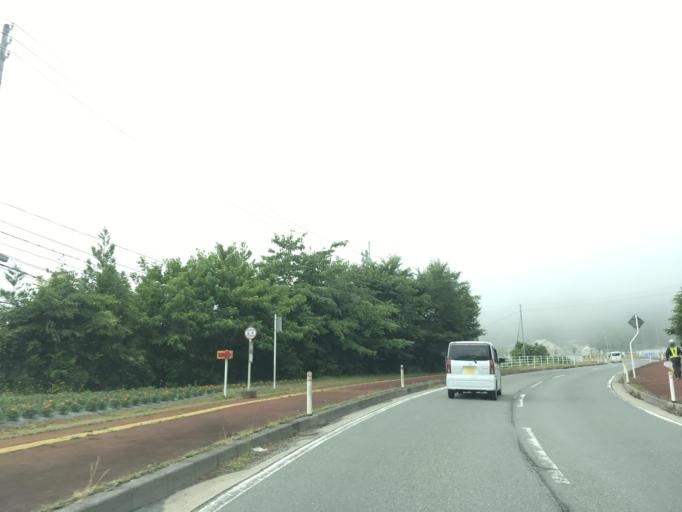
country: JP
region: Iwate
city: Ofunato
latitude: 38.9232
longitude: 141.6407
